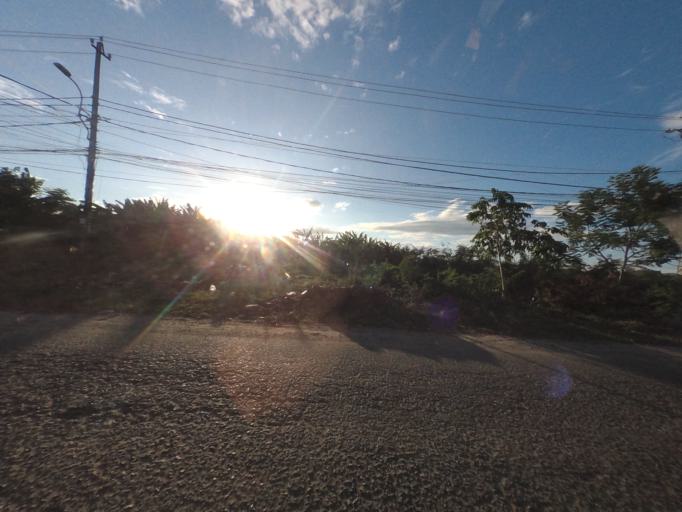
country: VN
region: Thua Thien-Hue
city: Hue
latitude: 16.4906
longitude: 107.5832
